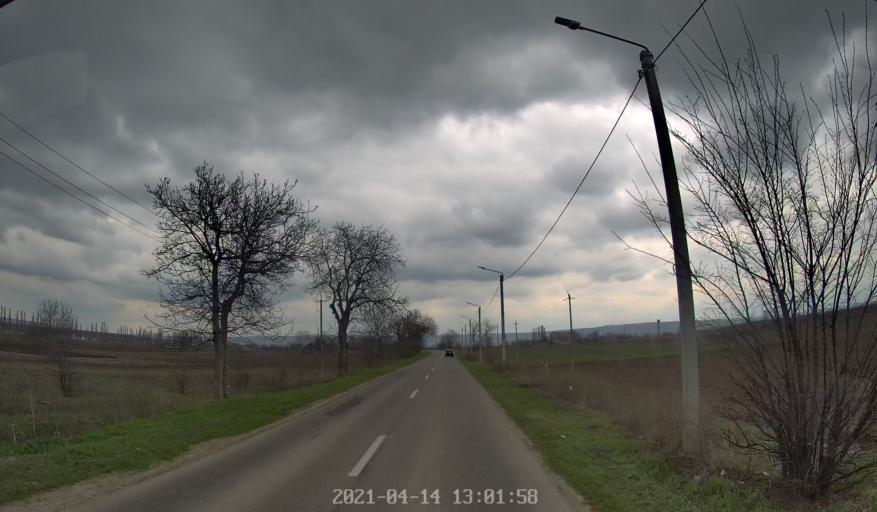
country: MD
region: Chisinau
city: Vadul lui Voda
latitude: 47.1272
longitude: 29.1129
